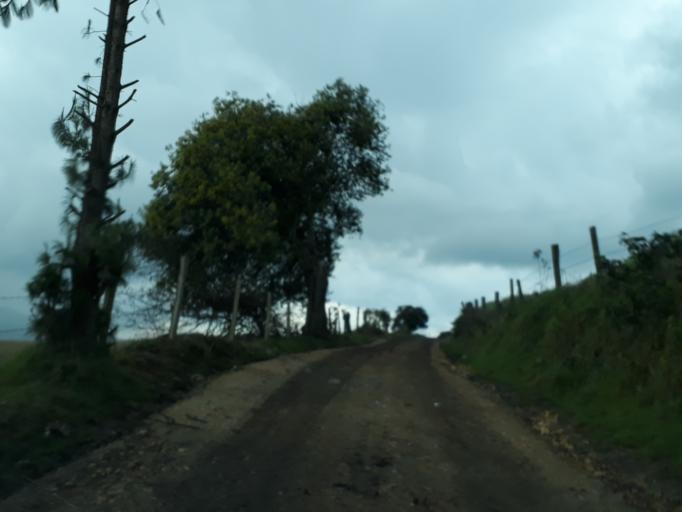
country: CO
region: Cundinamarca
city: Villapinzon
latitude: 5.2823
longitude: -73.6347
